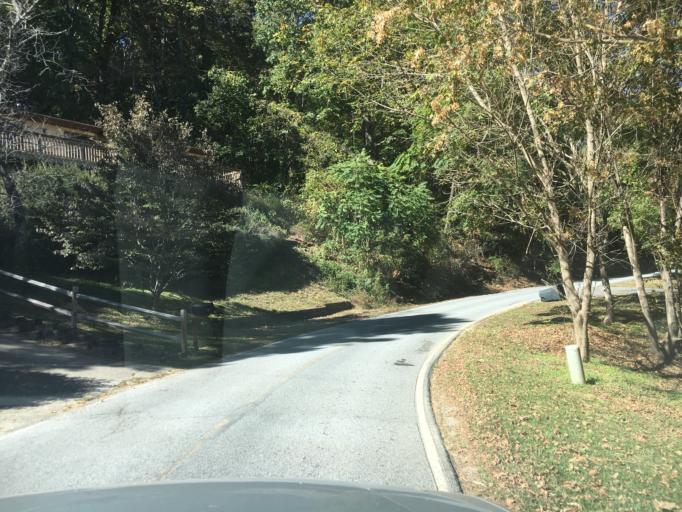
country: US
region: North Carolina
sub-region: Buncombe County
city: Woodfin
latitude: 35.6487
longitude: -82.5855
